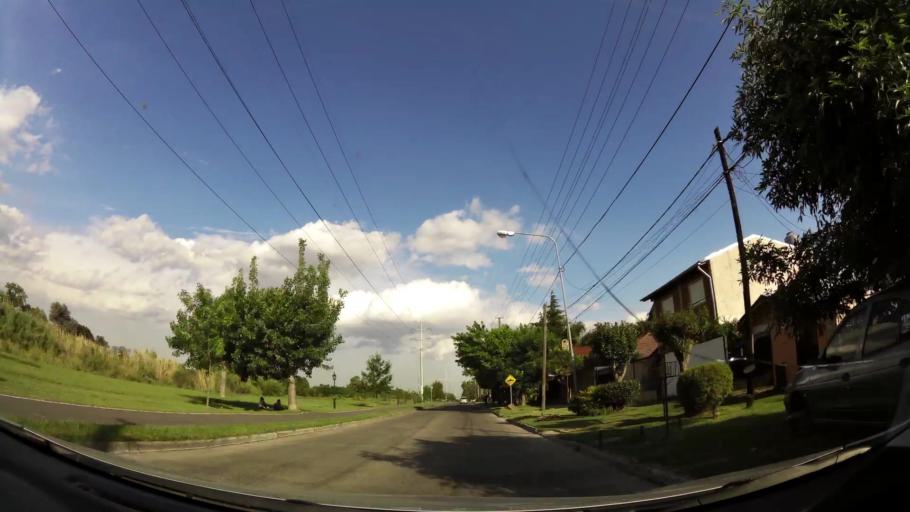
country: AR
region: Buenos Aires
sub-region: Partido de Tigre
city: Tigre
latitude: -34.4664
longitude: -58.6384
